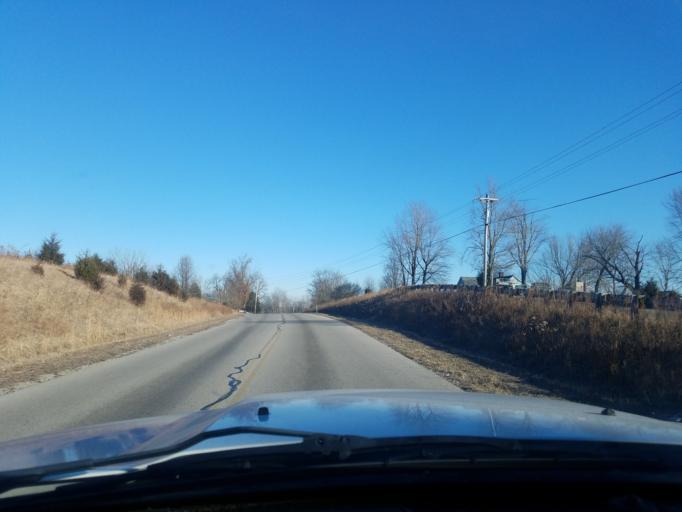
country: US
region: Kentucky
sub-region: Ohio County
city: Beaver Dam
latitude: 37.3678
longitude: -86.8369
